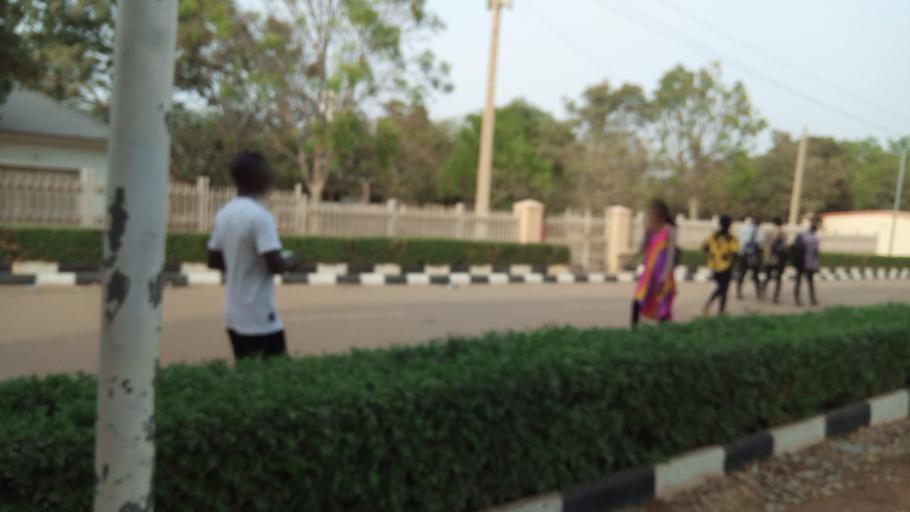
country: NG
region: Gombe
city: Gombe
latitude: 10.3067
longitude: 11.1715
